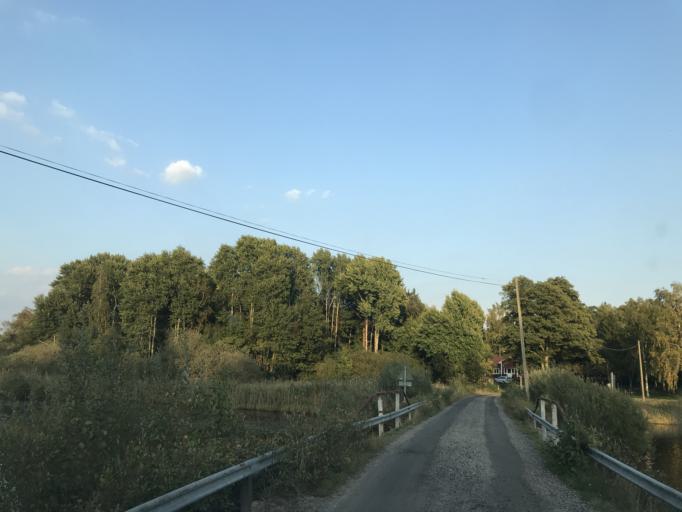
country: SE
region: Kronoberg
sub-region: Almhults Kommun
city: AElmhult
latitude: 56.6595
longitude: 14.1851
